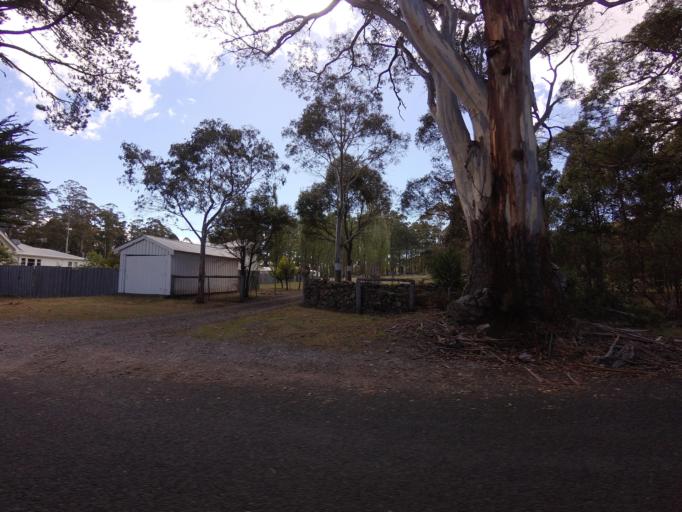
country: AU
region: Tasmania
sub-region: Break O'Day
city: St Helens
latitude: -41.6270
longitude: 148.2263
